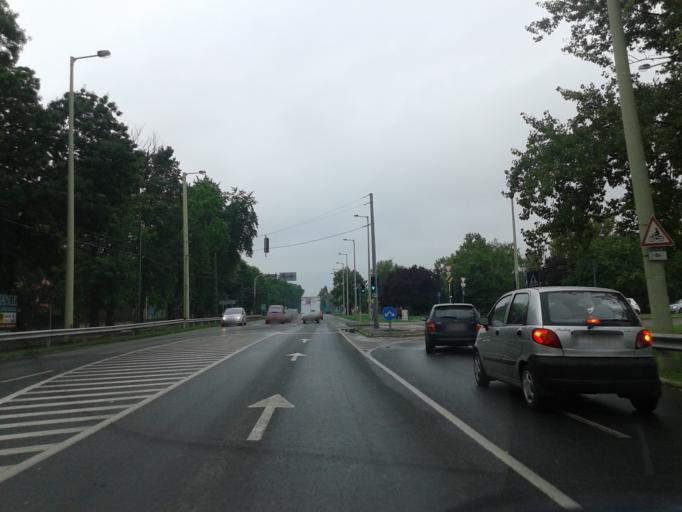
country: HU
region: Csongrad
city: Szeged
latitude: 46.2420
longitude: 20.1252
